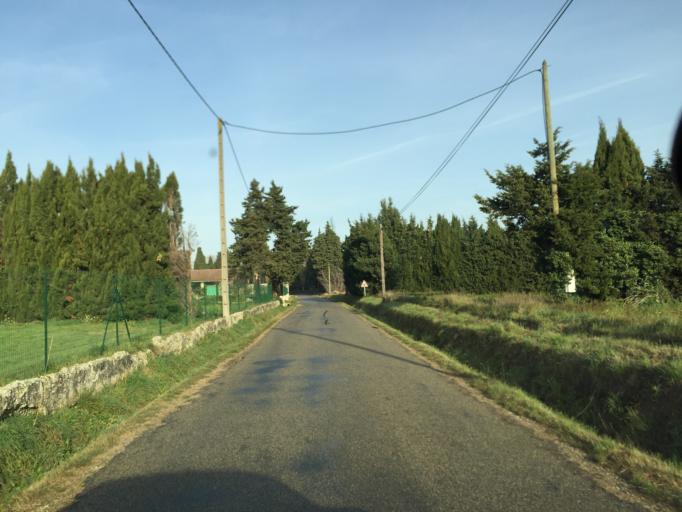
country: FR
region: Provence-Alpes-Cote d'Azur
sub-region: Departement du Vaucluse
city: Orange
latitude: 44.1461
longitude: 4.7863
